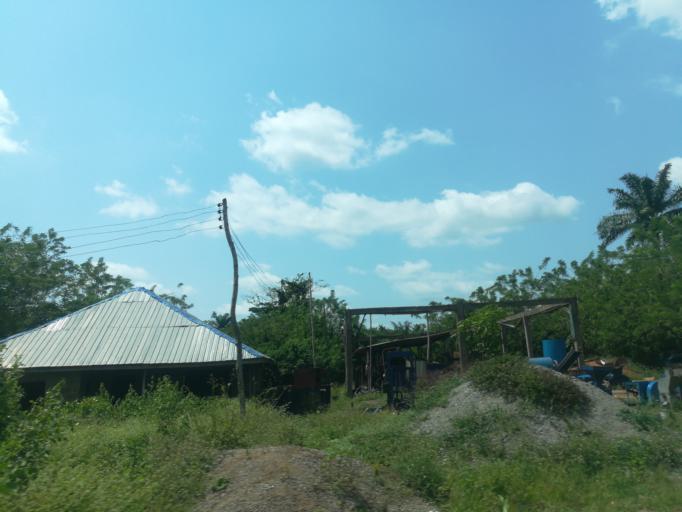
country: NG
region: Oyo
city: Moniya
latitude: 7.5636
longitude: 3.9096
